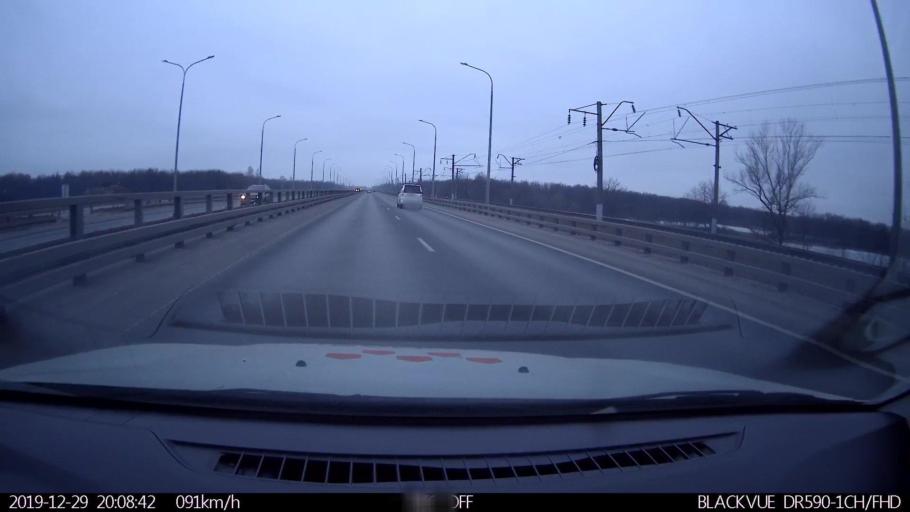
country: RU
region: Nizjnij Novgorod
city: Neklyudovo
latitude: 56.3824
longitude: 43.9619
